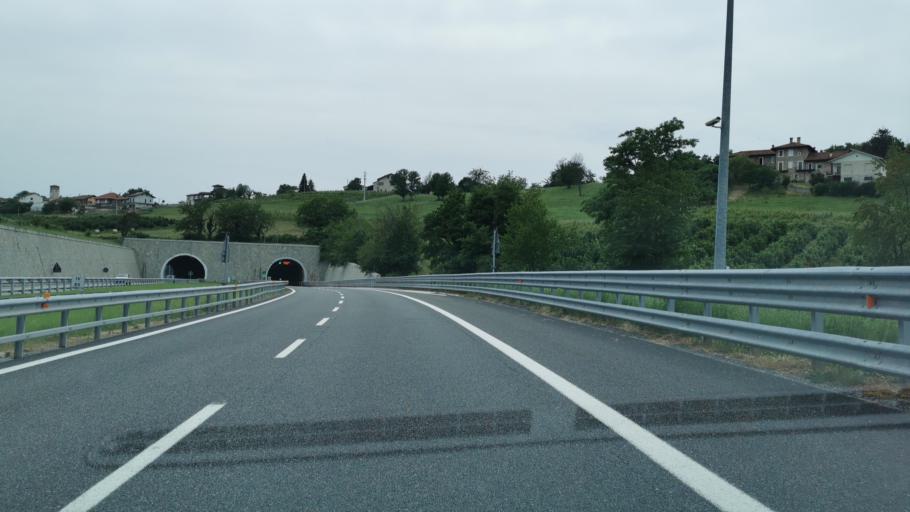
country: IT
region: Piedmont
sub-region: Provincia di Cuneo
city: Bastia Mondovi
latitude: 44.4235
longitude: 7.8811
